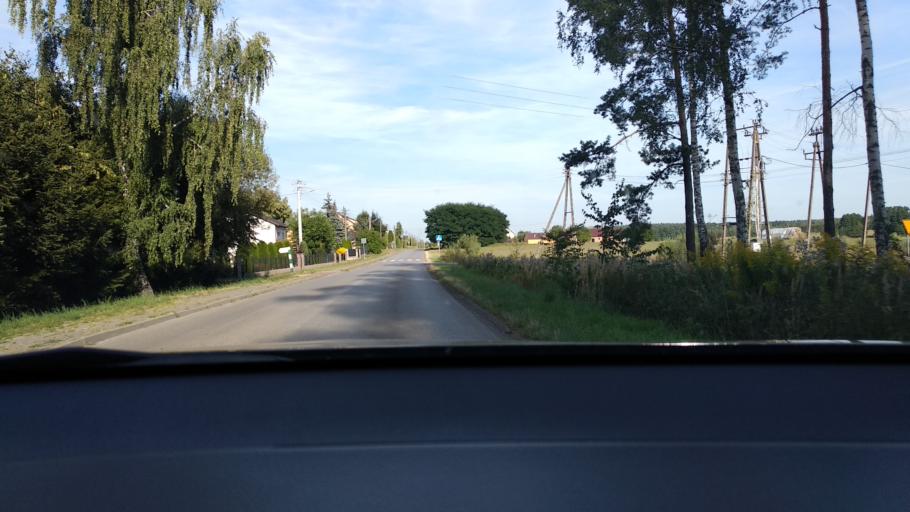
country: PL
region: Masovian Voivodeship
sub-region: Powiat pultuski
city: Obryte
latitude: 52.7141
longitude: 21.1789
